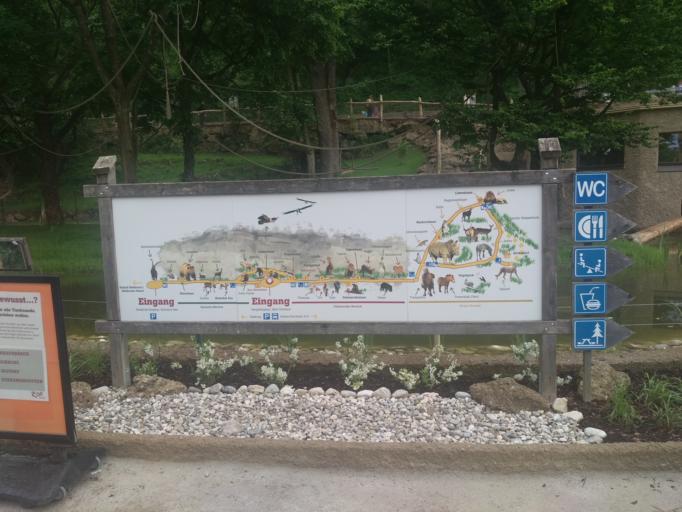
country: AT
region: Salzburg
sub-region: Politischer Bezirk Salzburg-Umgebung
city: Anif
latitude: 47.7570
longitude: 13.0642
